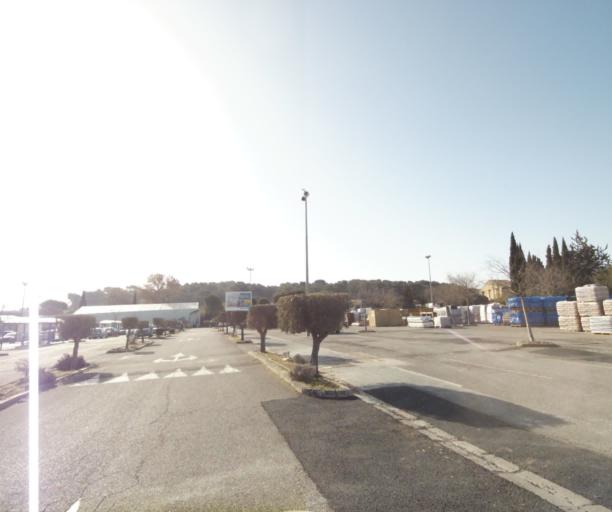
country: FR
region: Provence-Alpes-Cote d'Azur
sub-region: Departement des Bouches-du-Rhone
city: Septemes-les-Vallons
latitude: 43.4148
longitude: 5.3573
